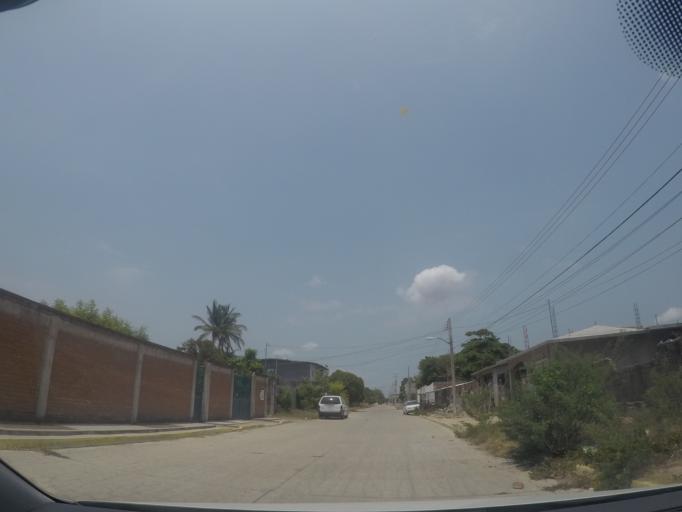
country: MX
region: Oaxaca
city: Asuncion Ixtaltepec
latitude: 16.5066
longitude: -95.0607
